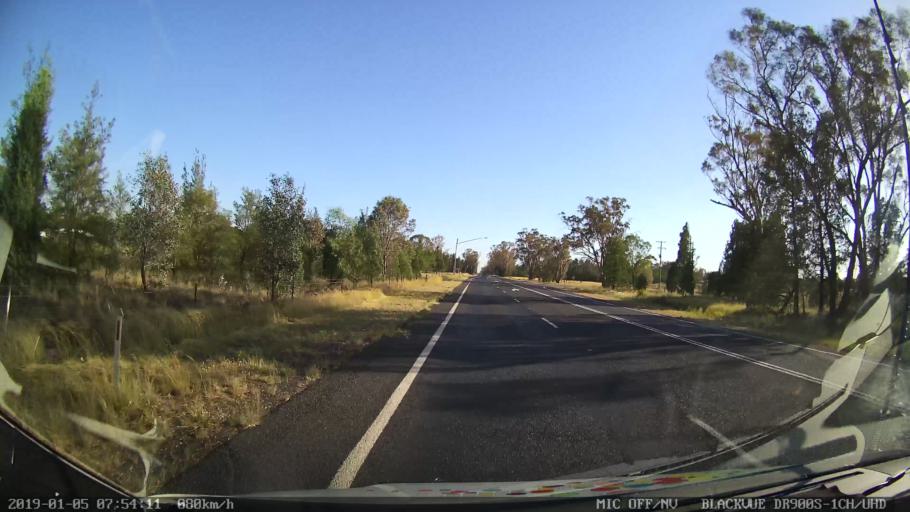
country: AU
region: New South Wales
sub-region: Gilgandra
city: Gilgandra
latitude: -31.7359
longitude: 148.6475
